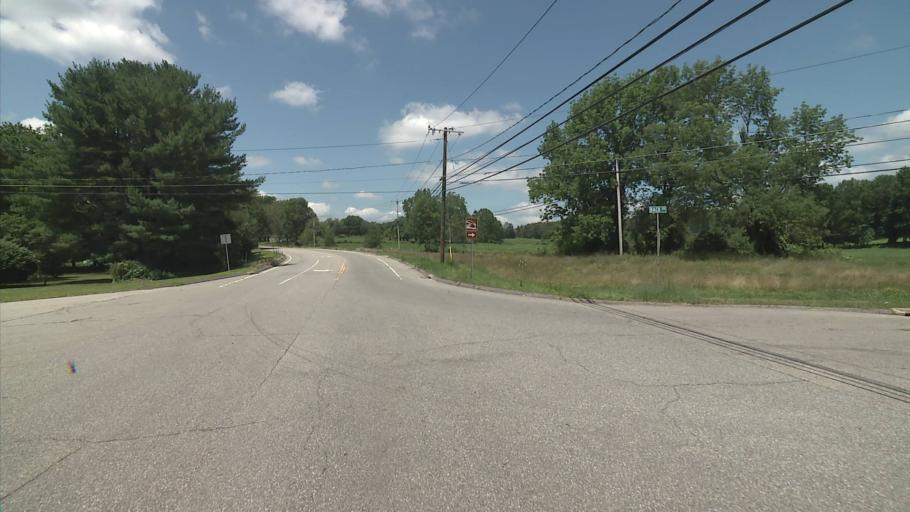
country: US
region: Connecticut
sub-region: Windham County
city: Windham
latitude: 41.7007
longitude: -72.1442
